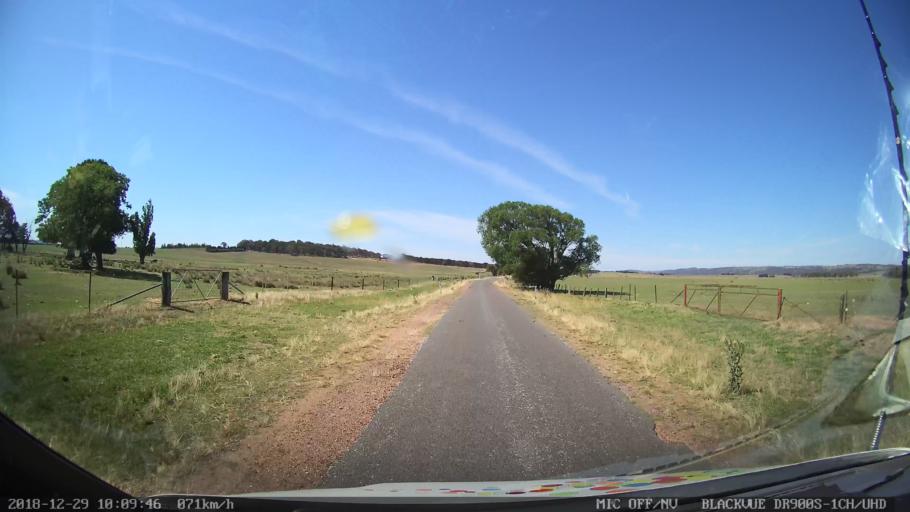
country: AU
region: New South Wales
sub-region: Yass Valley
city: Gundaroo
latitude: -34.8692
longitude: 149.4592
